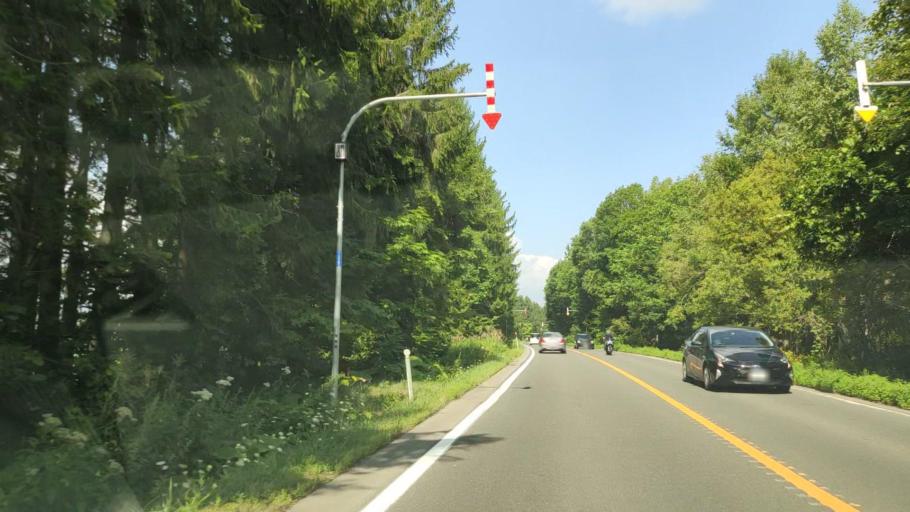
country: JP
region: Hokkaido
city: Shimo-furano
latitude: 43.5104
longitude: 142.4529
